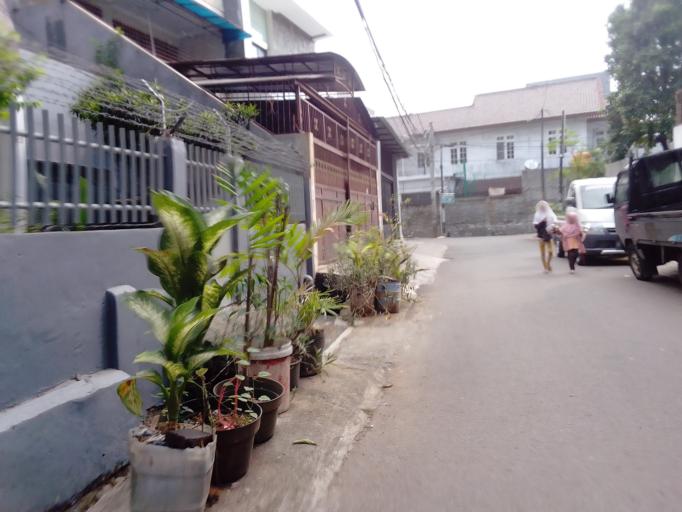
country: ID
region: Jakarta Raya
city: Jakarta
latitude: -6.1645
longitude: 106.8125
